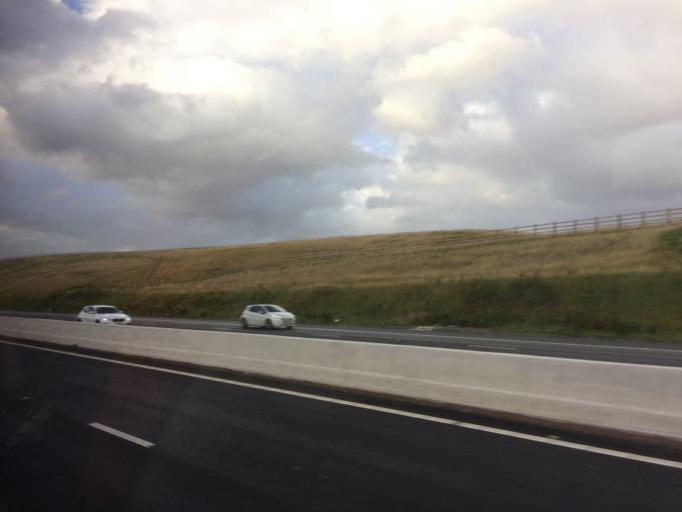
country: GB
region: Scotland
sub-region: North Lanarkshire
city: Coatbridge
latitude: 55.8414
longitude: -4.0447
